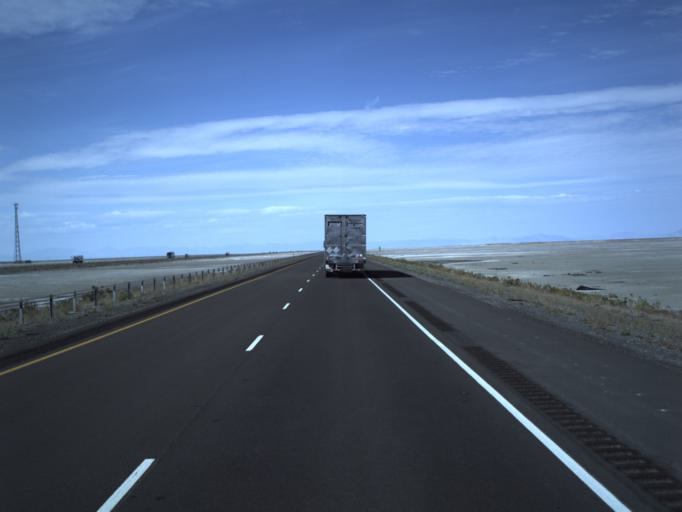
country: US
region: Utah
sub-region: Tooele County
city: Wendover
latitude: 40.7283
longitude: -113.3187
